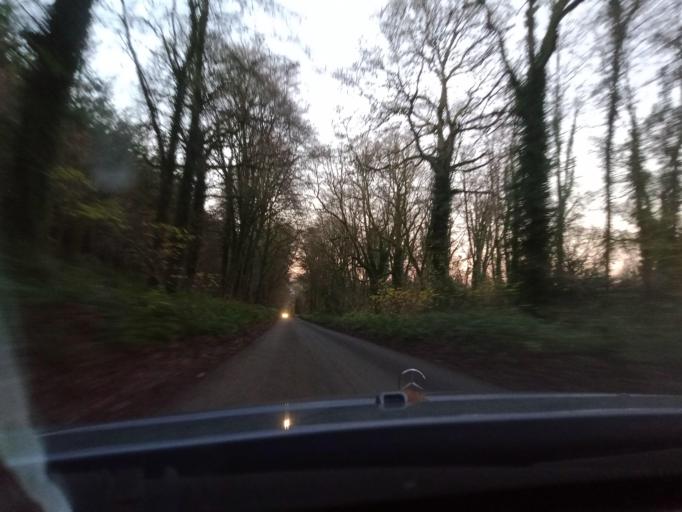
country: IE
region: Leinster
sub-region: Kilkenny
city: Thomastown
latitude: 52.5086
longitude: -7.1287
